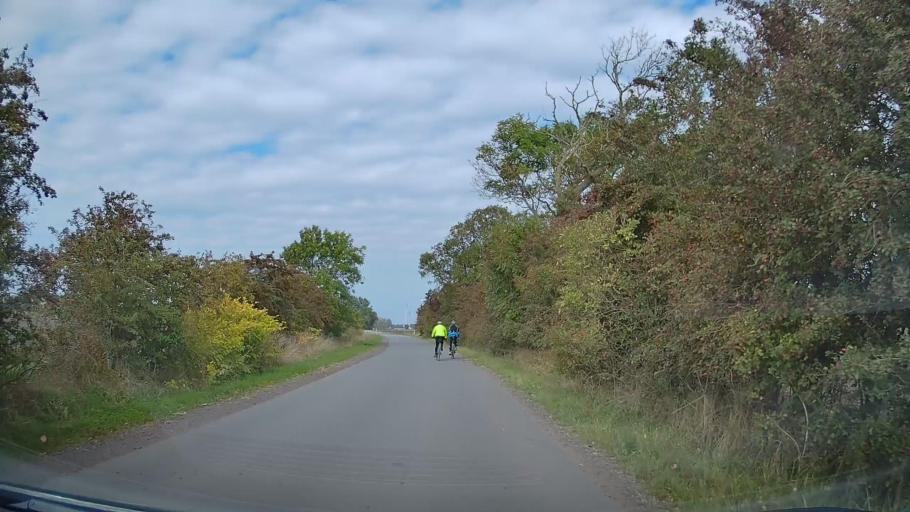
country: DE
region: Schleswig-Holstein
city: Grossenbrode
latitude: 54.4996
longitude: 11.0600
